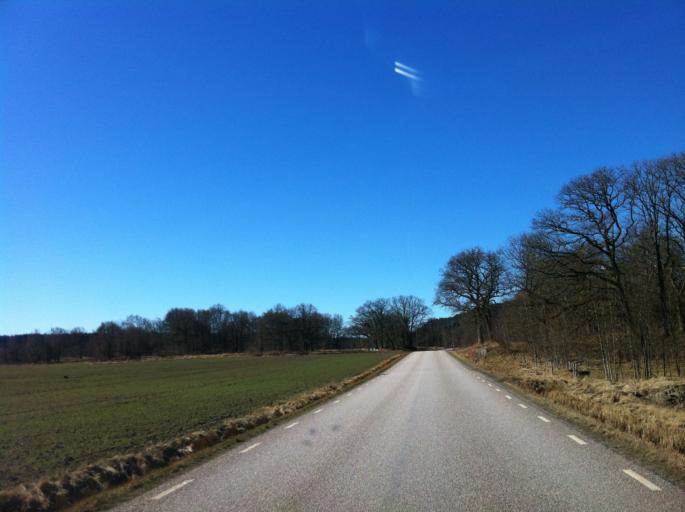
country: SE
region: Vaestra Goetaland
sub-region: Grastorps Kommun
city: Graestorp
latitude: 58.4205
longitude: 12.6063
